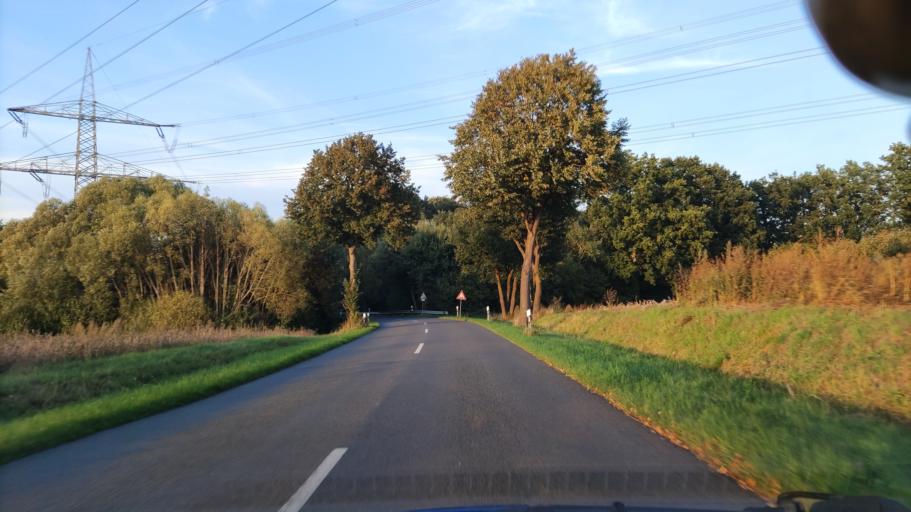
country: DE
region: Lower Saxony
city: Gerdau
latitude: 52.9883
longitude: 10.3791
